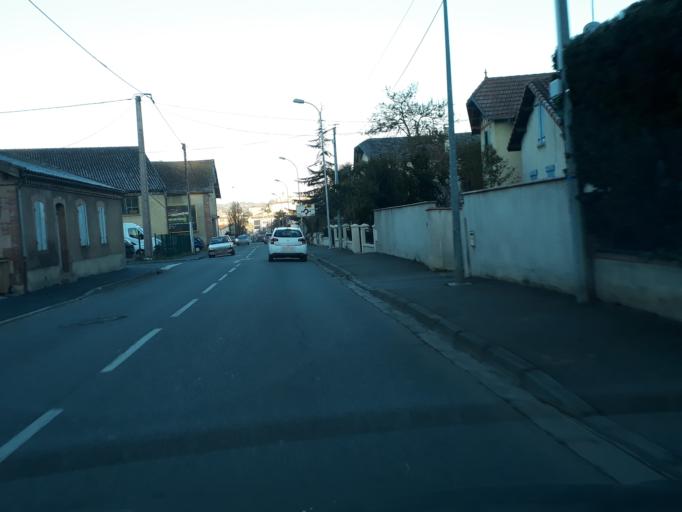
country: FR
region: Midi-Pyrenees
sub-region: Departement du Gers
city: Auch
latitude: 43.6401
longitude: 0.5980
